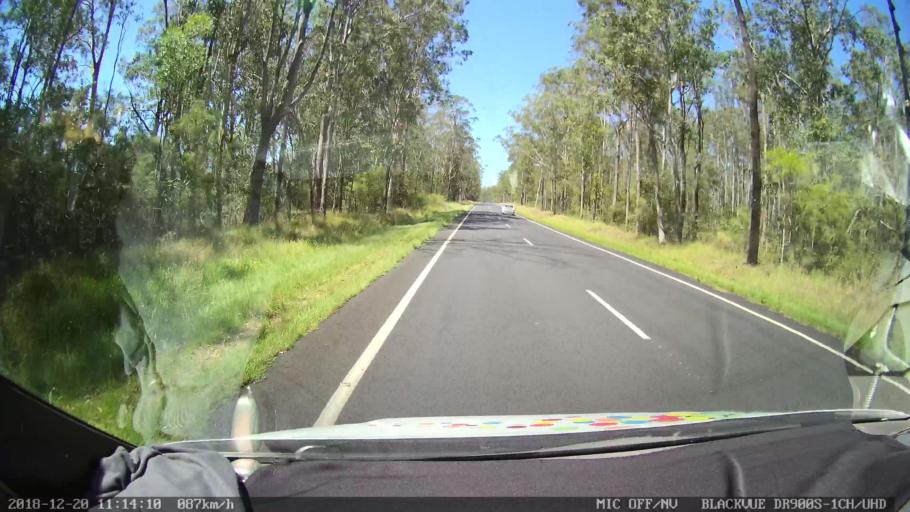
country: AU
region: New South Wales
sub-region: Richmond Valley
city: Casino
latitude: -28.9972
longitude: 153.0101
